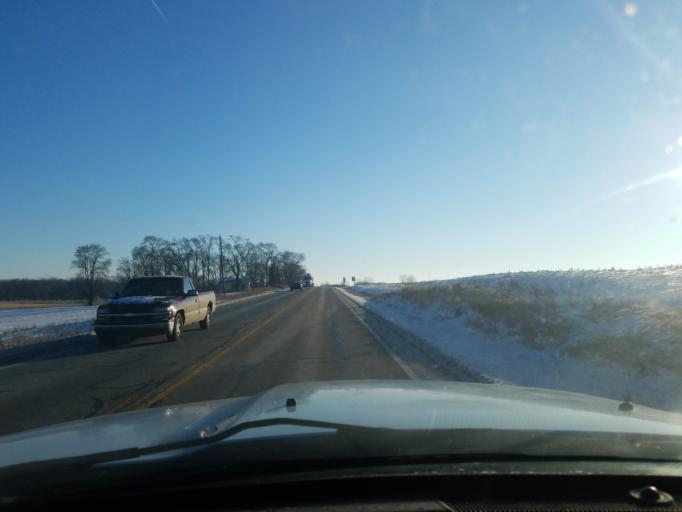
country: US
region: Indiana
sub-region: Noble County
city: Ligonier
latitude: 41.4524
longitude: -85.5663
